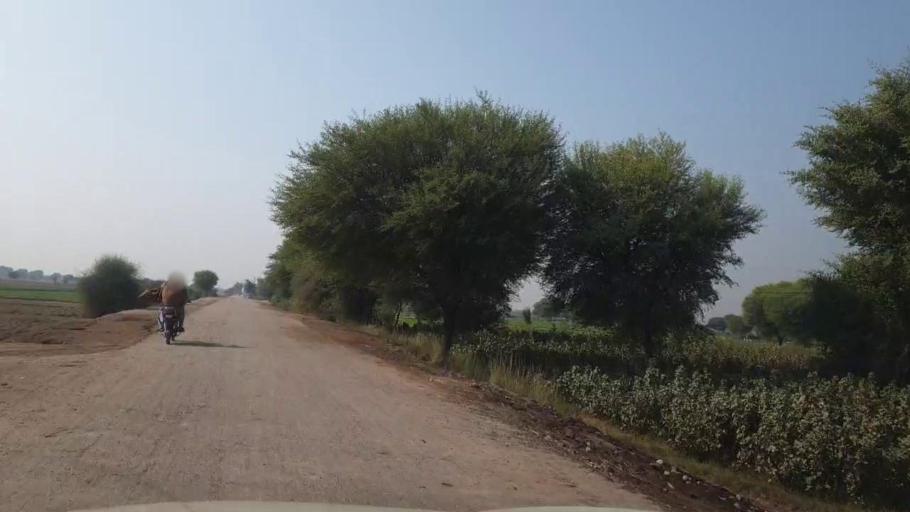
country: PK
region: Sindh
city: Bhan
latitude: 26.5146
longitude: 67.7994
